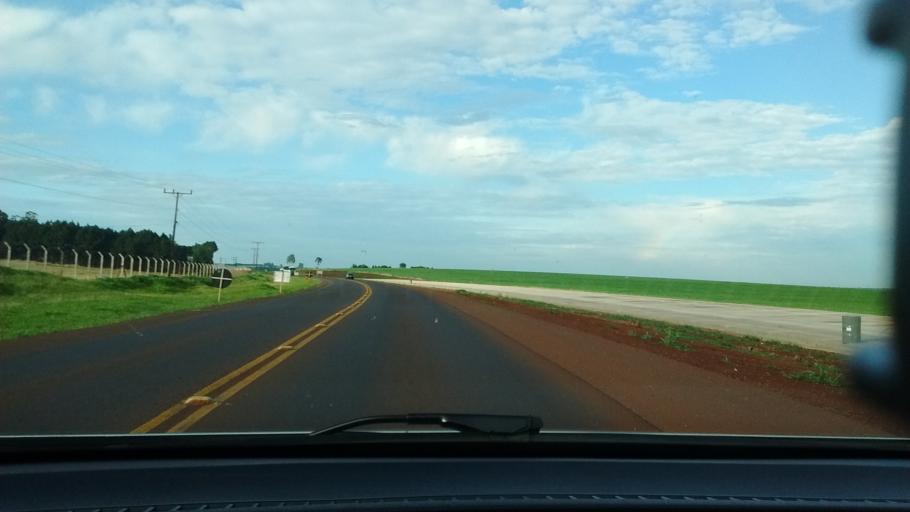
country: BR
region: Parana
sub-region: Cascavel
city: Cascavel
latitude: -25.0849
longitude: -53.5883
